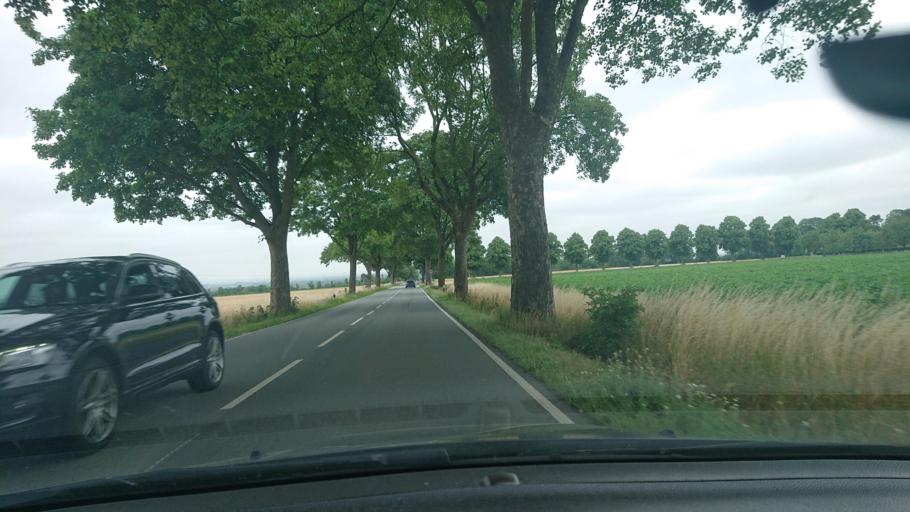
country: DE
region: North Rhine-Westphalia
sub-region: Regierungsbezirk Arnsberg
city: Soest
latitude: 51.5378
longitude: 8.0980
